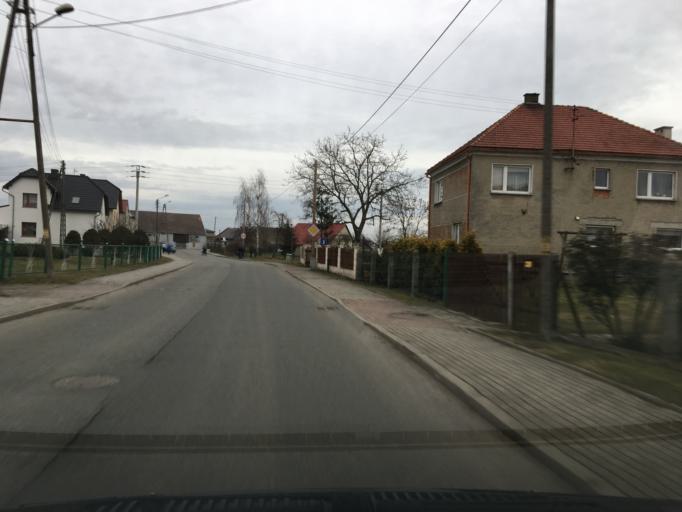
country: PL
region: Opole Voivodeship
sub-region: Powiat kedzierzynsko-kozielski
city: Kozle
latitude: 50.3552
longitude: 18.1244
